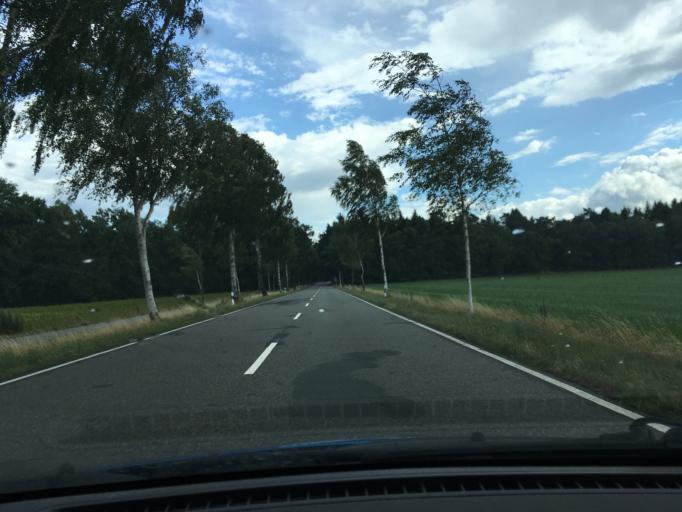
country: DE
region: Lower Saxony
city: Wietzendorf
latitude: 52.9825
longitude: 9.9417
